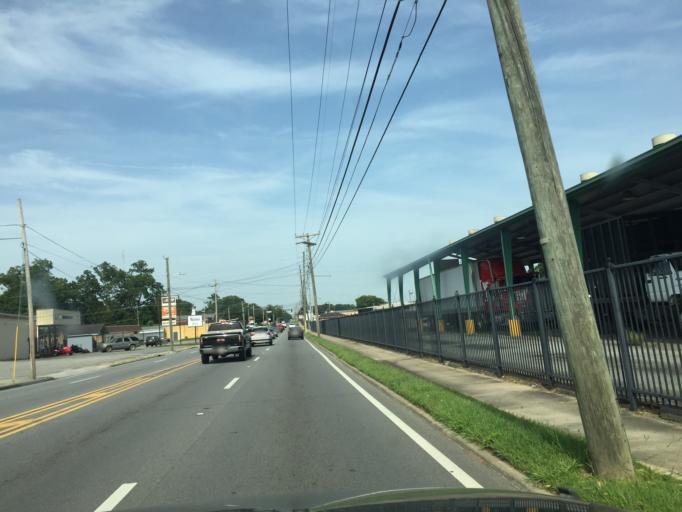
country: US
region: Georgia
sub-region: Thomas County
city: Thomasville
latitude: 30.8356
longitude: -83.9714
